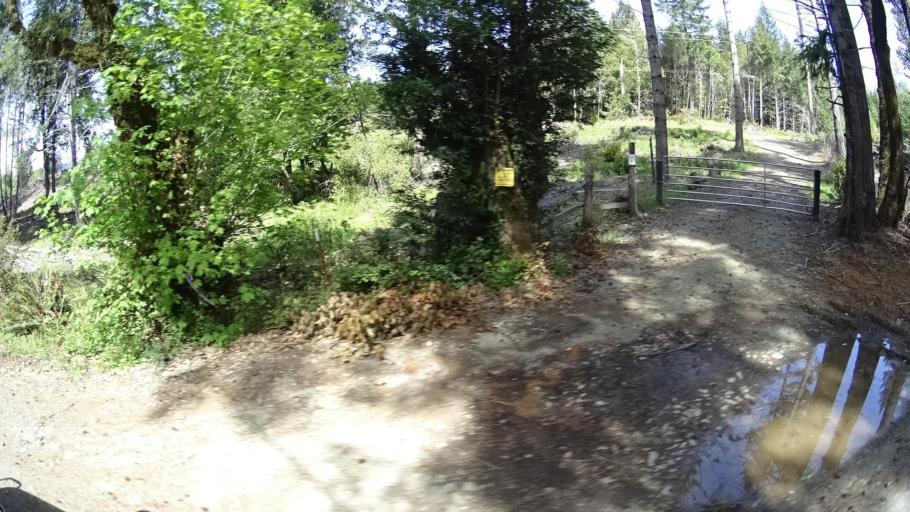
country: US
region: California
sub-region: Humboldt County
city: Redway
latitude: 40.3754
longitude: -123.7406
